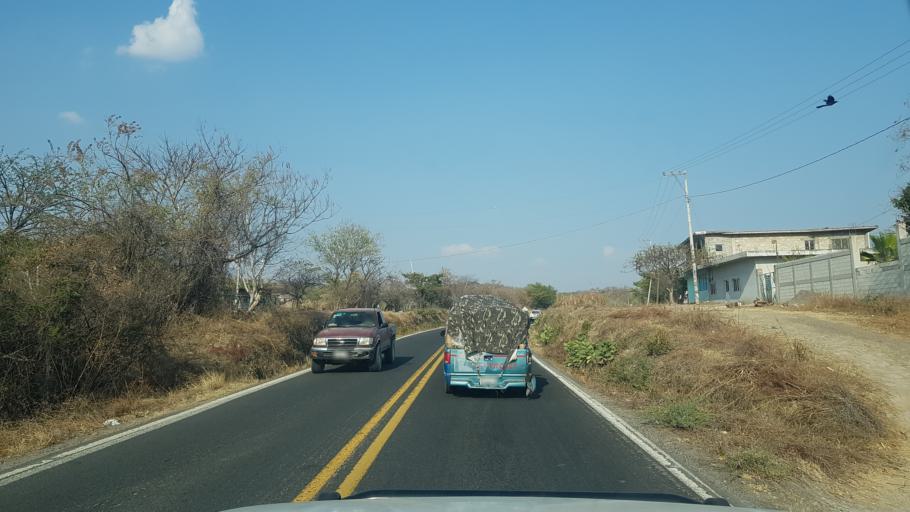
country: MX
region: Puebla
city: Calmeca
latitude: 18.6435
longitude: -98.6342
